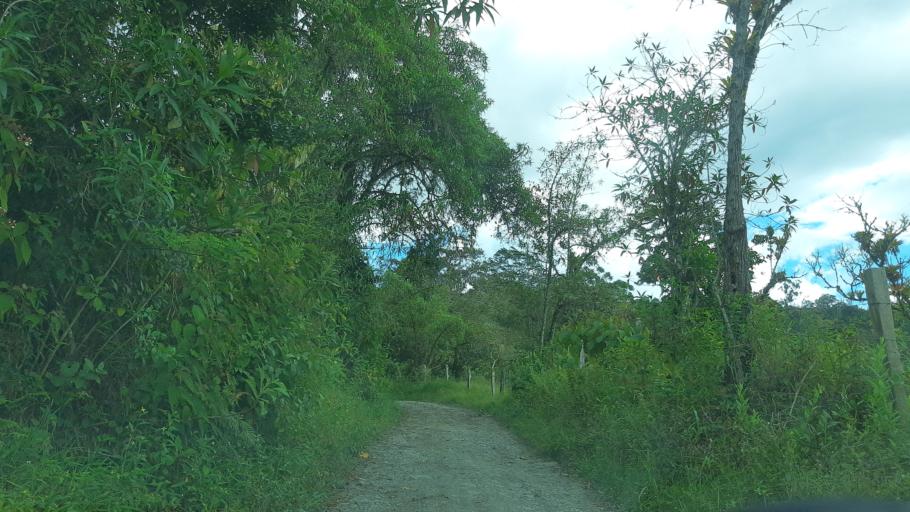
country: CO
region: Boyaca
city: Garagoa
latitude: 5.0390
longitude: -73.3314
